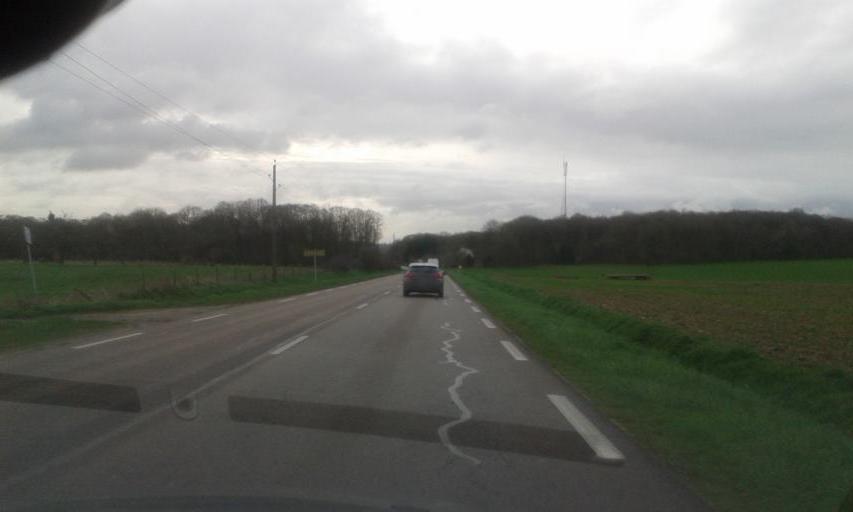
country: FR
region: Haute-Normandie
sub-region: Departement de l'Eure
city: Fleury-sur-Andelle
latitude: 49.3749
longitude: 1.3301
